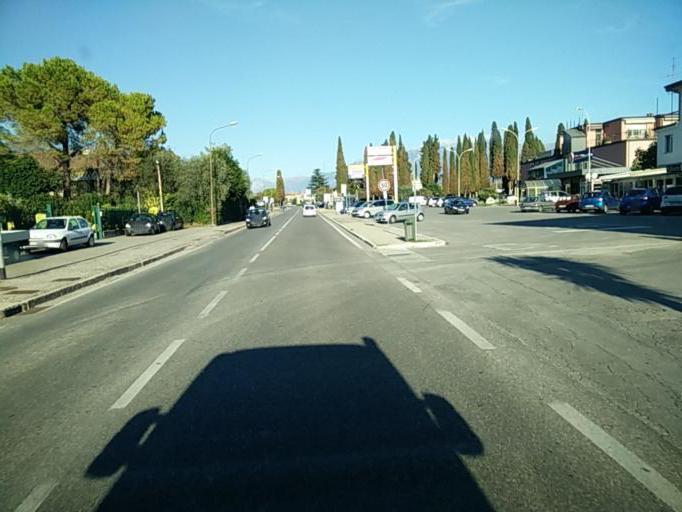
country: IT
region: Lombardy
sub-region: Provincia di Brescia
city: Toscolano Maderno
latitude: 45.6360
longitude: 10.6035
